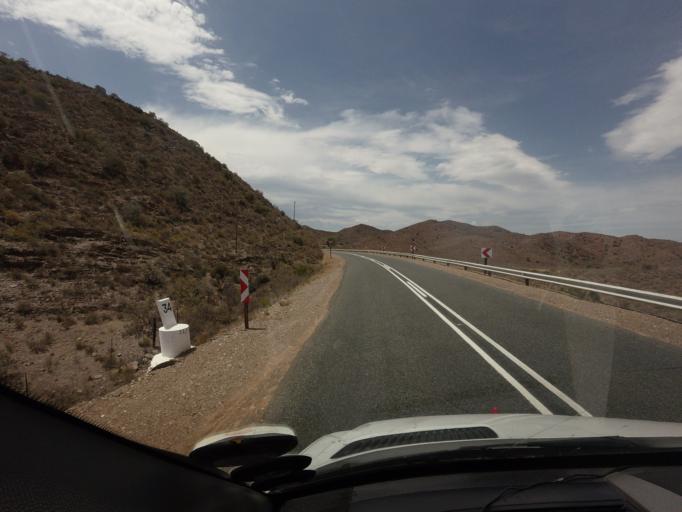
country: ZA
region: Western Cape
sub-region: Eden District Municipality
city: Ladismith
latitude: -33.7127
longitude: 20.9689
